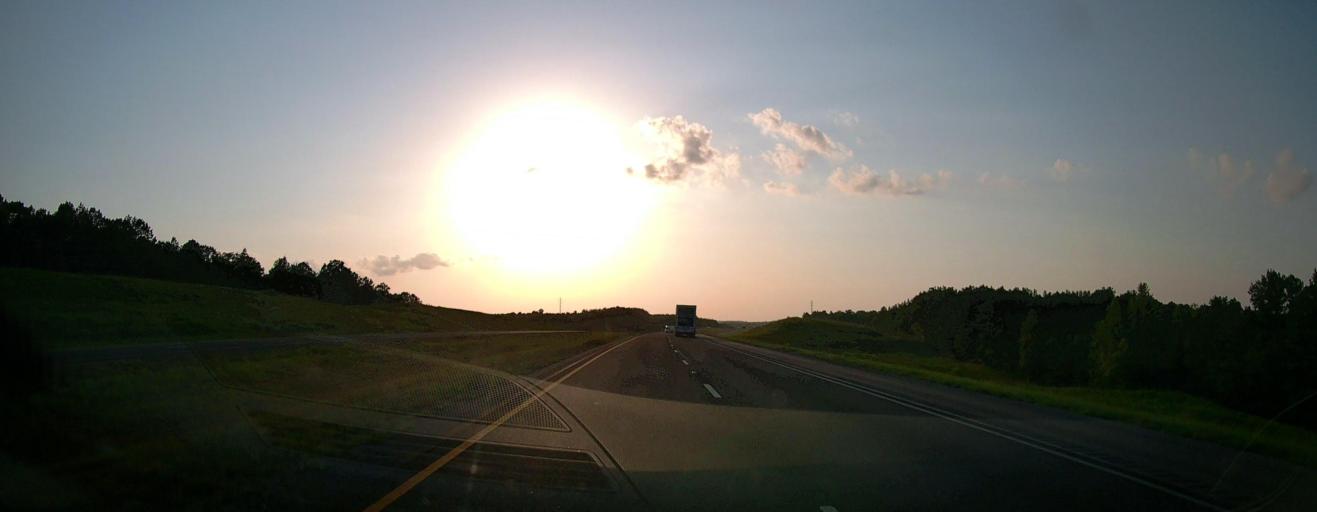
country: US
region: Alabama
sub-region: Marion County
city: Winfield
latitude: 33.9769
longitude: -87.7482
